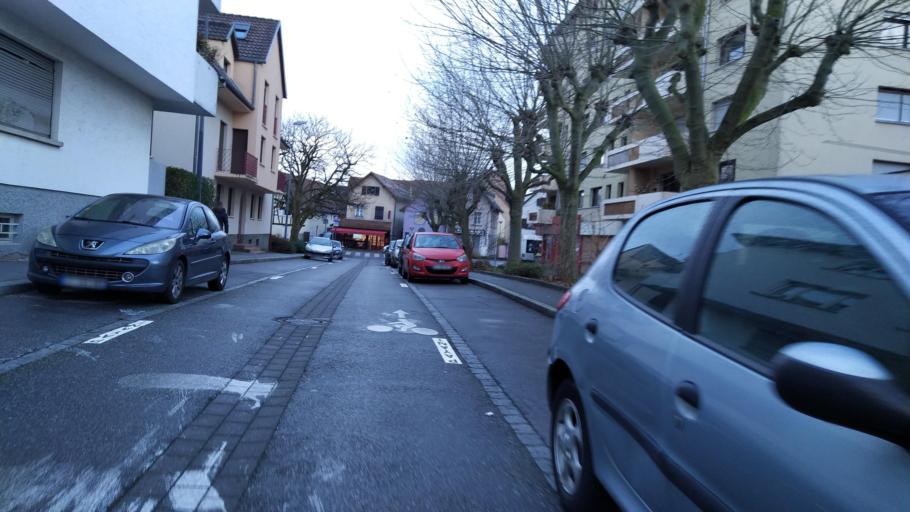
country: FR
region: Alsace
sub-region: Departement du Bas-Rhin
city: Schiltigheim
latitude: 48.6088
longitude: 7.7517
